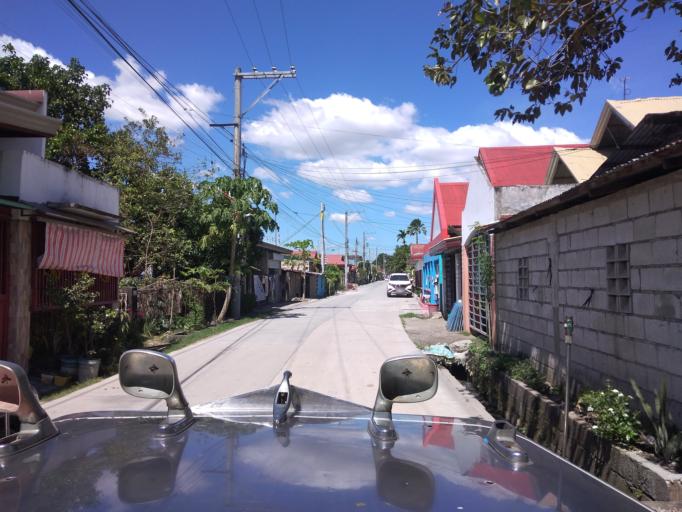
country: PH
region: Central Luzon
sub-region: Province of Pampanga
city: Magliman
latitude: 15.0435
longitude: 120.6436
